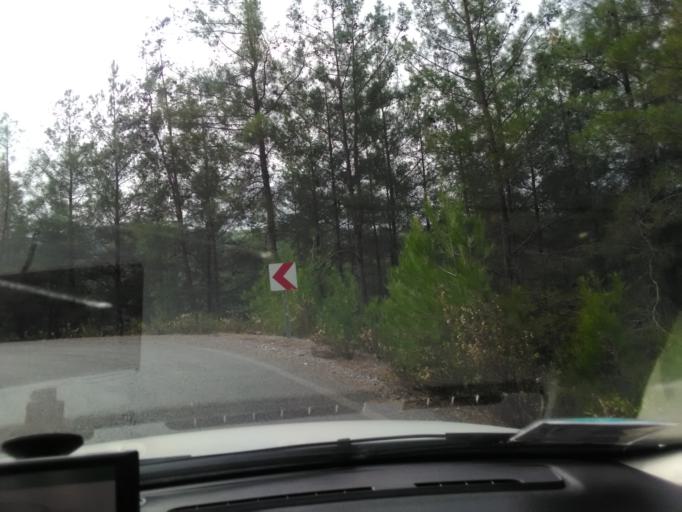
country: TR
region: Antalya
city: Gazipasa
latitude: 36.2400
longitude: 32.4195
